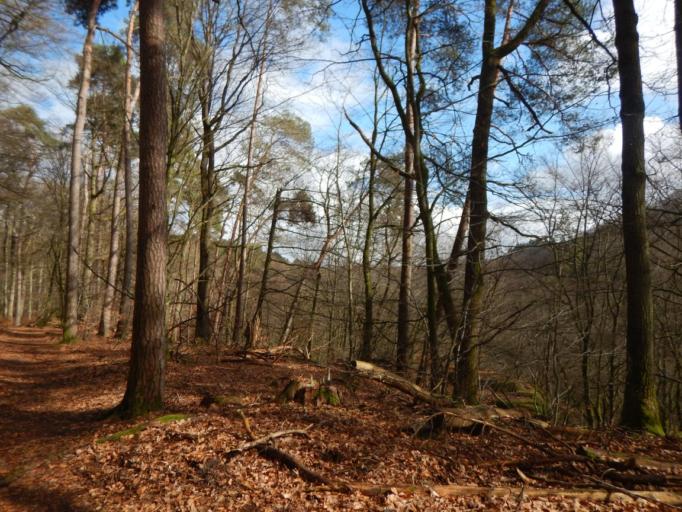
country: LU
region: Grevenmacher
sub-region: Canton d'Echternach
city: Beaufort
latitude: 49.8235
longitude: 6.2898
